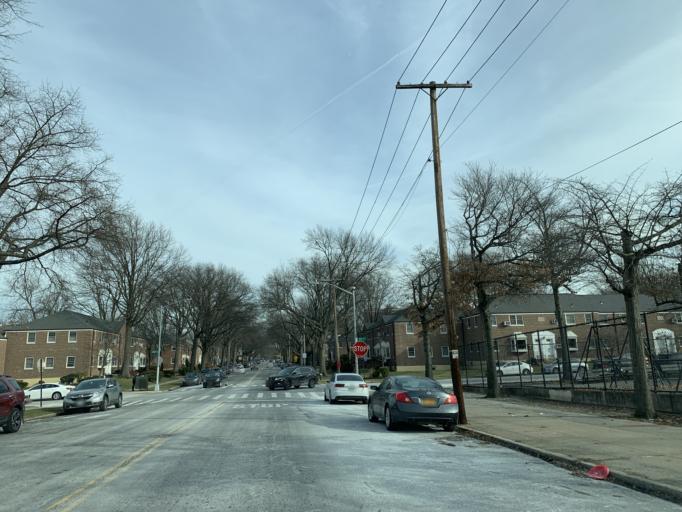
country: US
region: New York
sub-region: Nassau County
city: Lake Success
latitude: 40.7573
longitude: -73.7283
